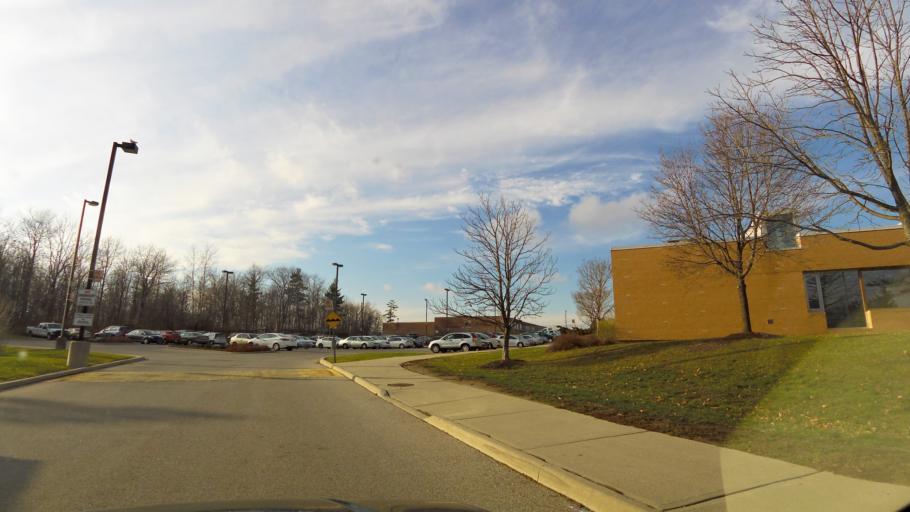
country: CA
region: Ontario
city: Mississauga
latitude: 43.5418
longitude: -79.6844
